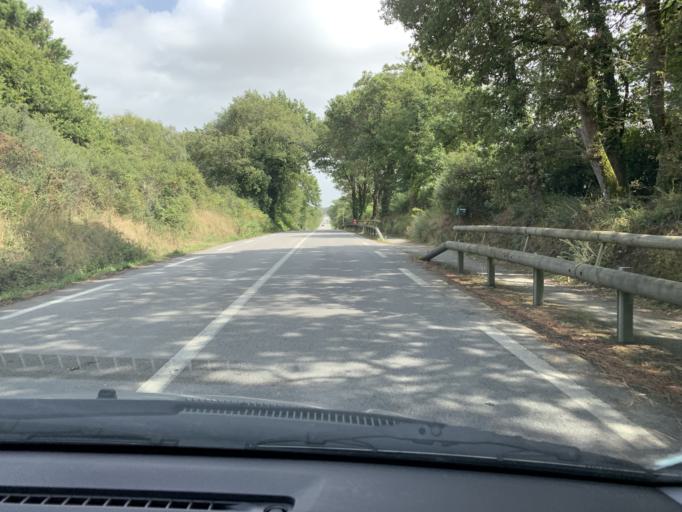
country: FR
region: Brittany
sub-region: Departement du Morbihan
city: Penestin
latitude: 47.4821
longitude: -2.4668
